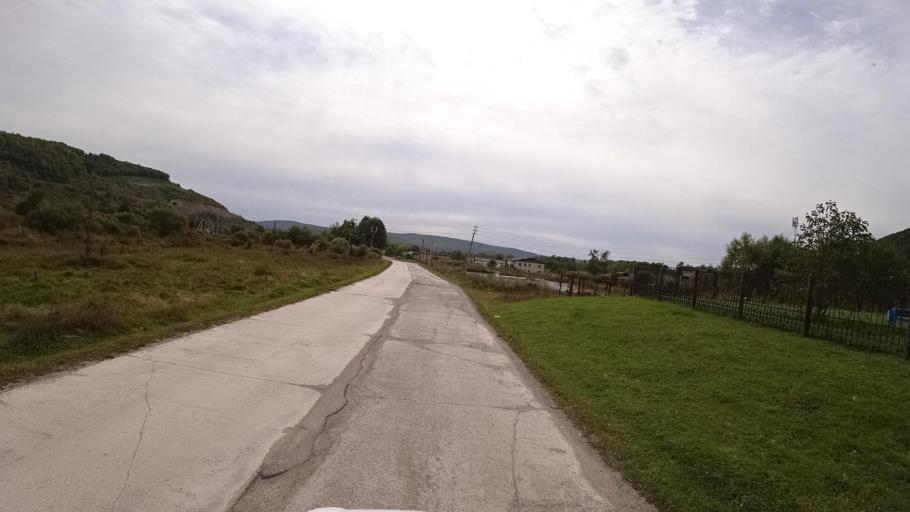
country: RU
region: Jewish Autonomous Oblast
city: Khingansk
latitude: 48.9957
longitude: 131.0510
